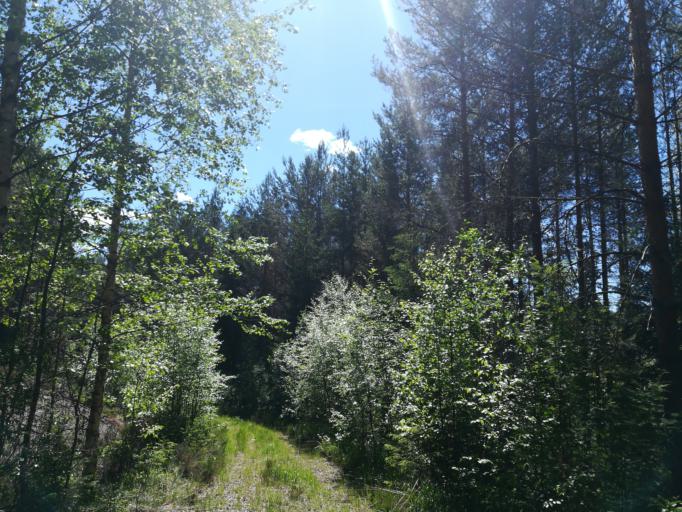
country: FI
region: Southern Savonia
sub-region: Mikkeli
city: Puumala
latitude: 61.6177
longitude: 28.1615
